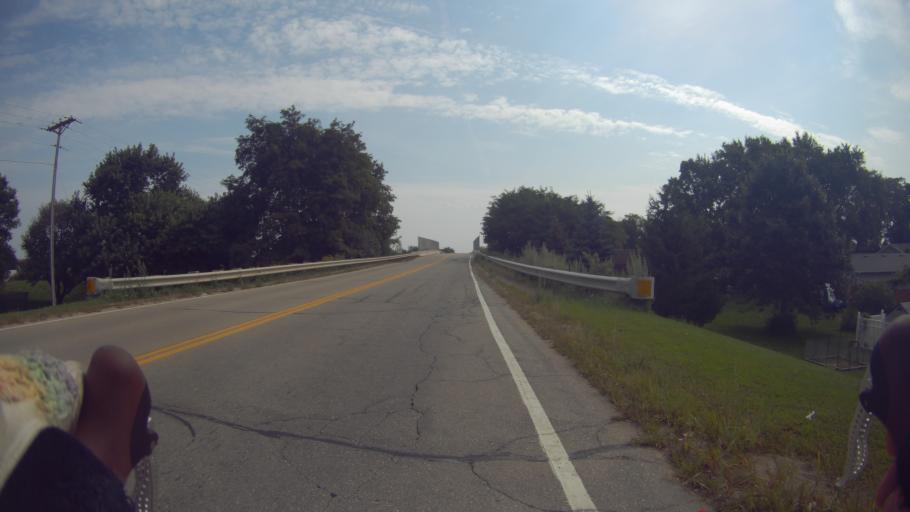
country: US
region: Wisconsin
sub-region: Dane County
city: Monona
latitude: 43.0992
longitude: -89.2871
